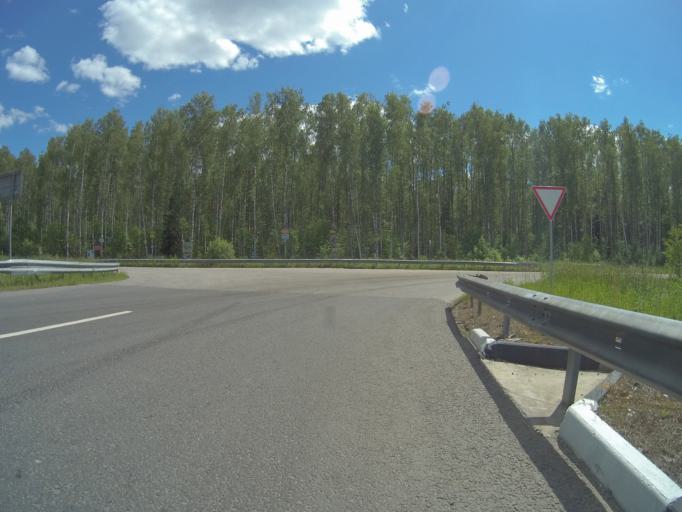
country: RU
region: Vladimir
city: Sudogda
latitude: 56.1025
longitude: 40.7739
